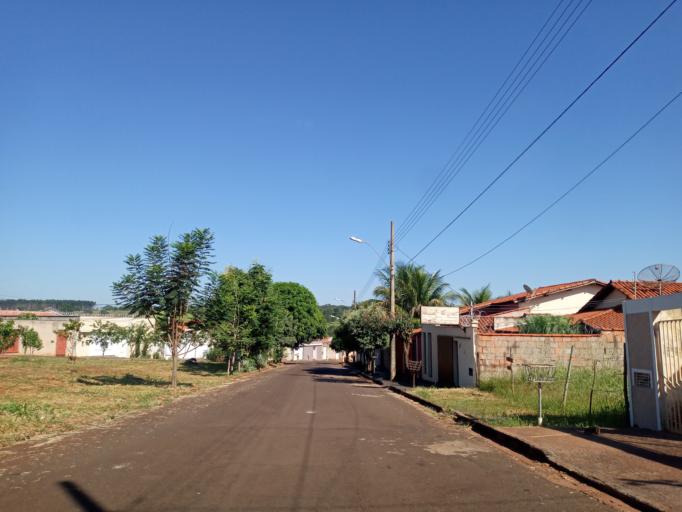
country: BR
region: Minas Gerais
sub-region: Ituiutaba
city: Ituiutaba
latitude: -18.9783
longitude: -49.4904
